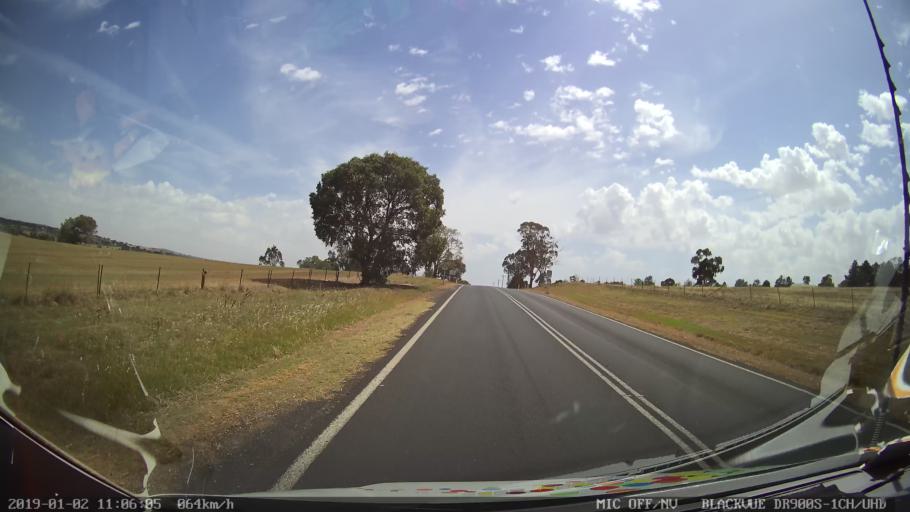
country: AU
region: New South Wales
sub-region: Young
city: Young
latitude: -34.5579
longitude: 148.3554
